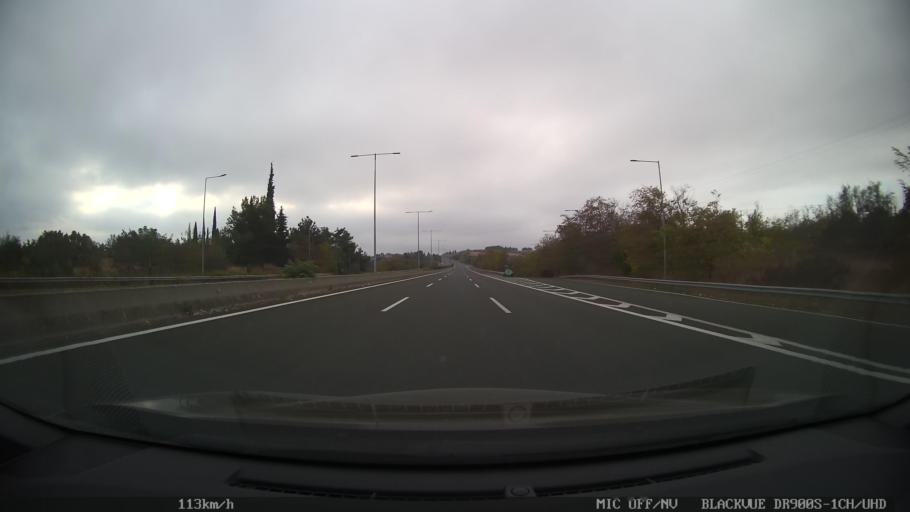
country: GR
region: Central Macedonia
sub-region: Nomos Pierias
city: Makrygialos
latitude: 40.4622
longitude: 22.5779
